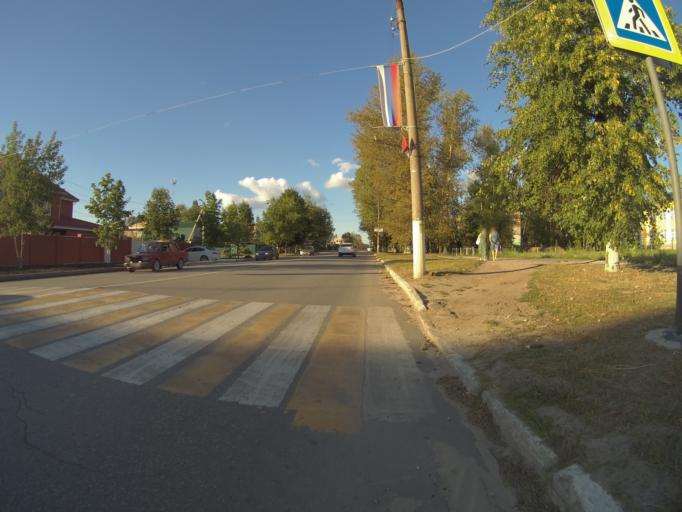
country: RU
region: Vladimir
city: Gus'-Khrustal'nyy
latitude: 55.6199
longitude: 40.6774
